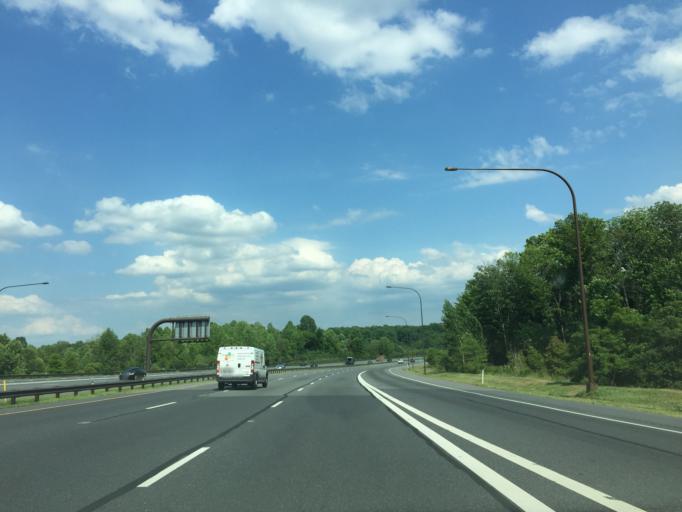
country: US
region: Maryland
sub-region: Montgomery County
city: Rossmoor
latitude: 39.1174
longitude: -77.0697
